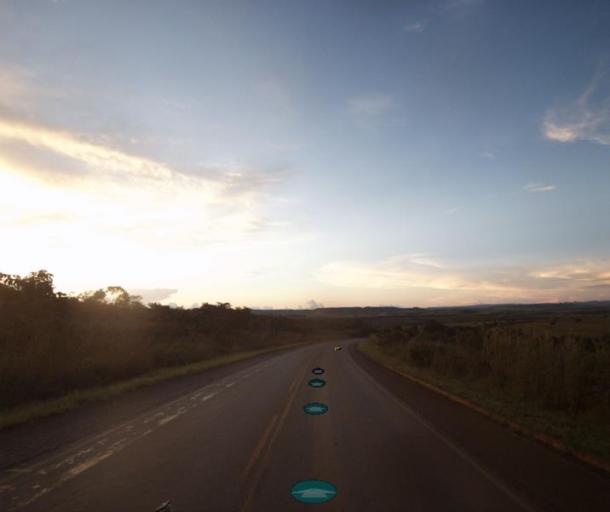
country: BR
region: Goias
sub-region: Pirenopolis
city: Pirenopolis
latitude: -16.0109
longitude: -48.8404
